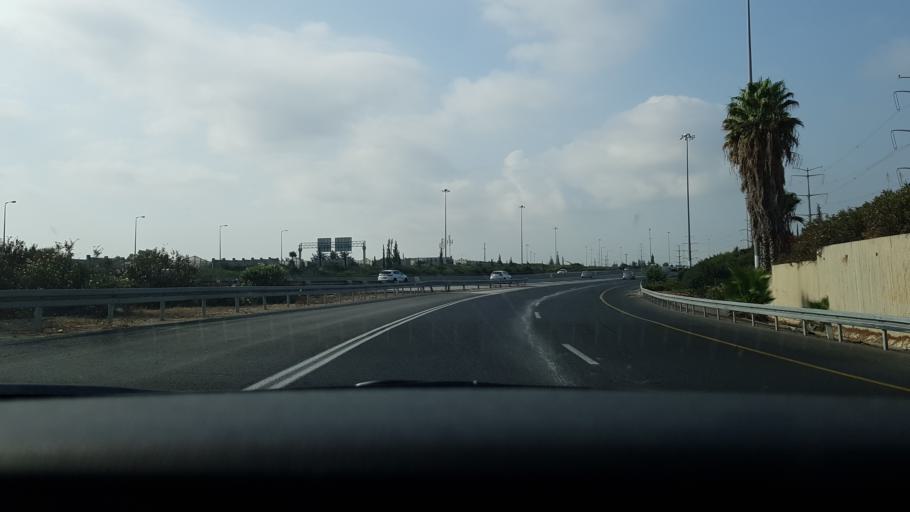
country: IL
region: Tel Aviv
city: Azor
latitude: 32.0154
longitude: 34.8187
